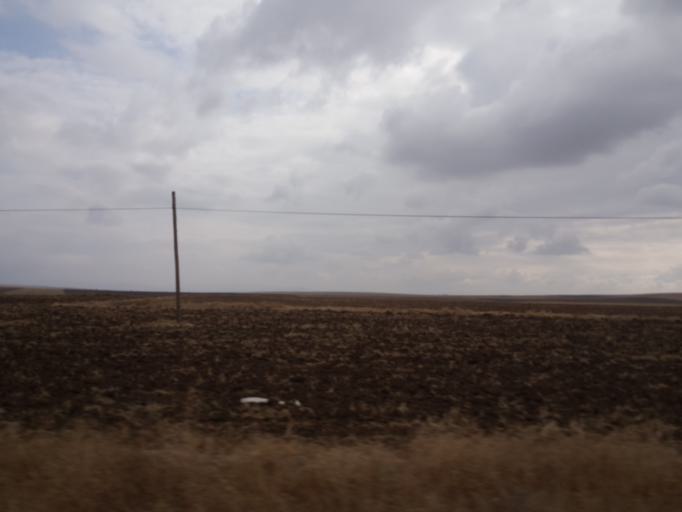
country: TR
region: Kirikkale
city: Celebi
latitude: 39.5604
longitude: 33.5767
